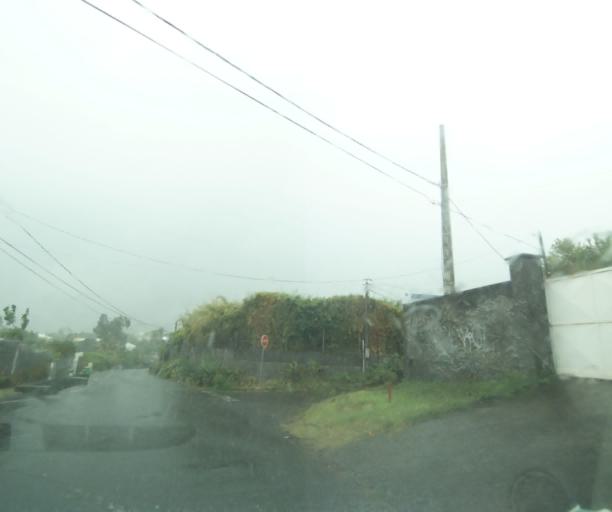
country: RE
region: Reunion
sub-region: Reunion
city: La Possession
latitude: -20.9858
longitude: 55.3250
